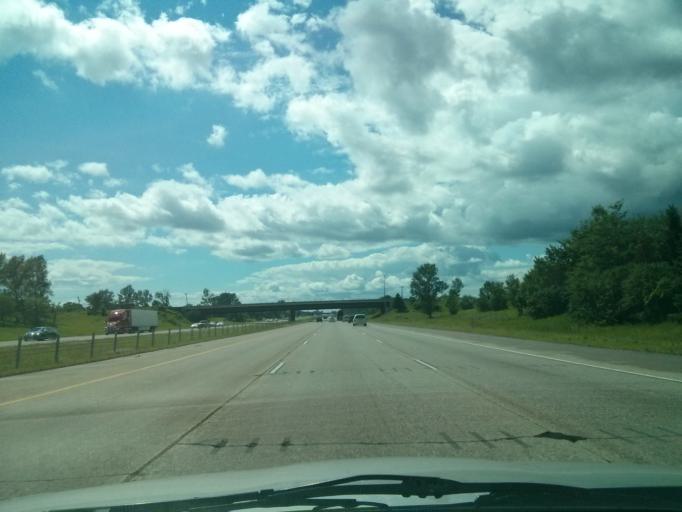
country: US
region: Minnesota
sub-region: Washington County
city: Lake Elmo
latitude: 44.9491
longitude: -92.8593
